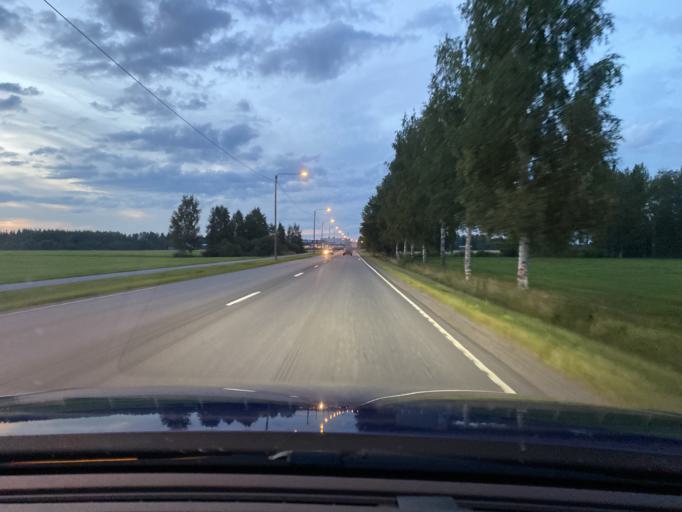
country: FI
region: Southern Ostrobothnia
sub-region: Suupohja
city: Kauhajoki
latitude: 62.4391
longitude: 22.2085
